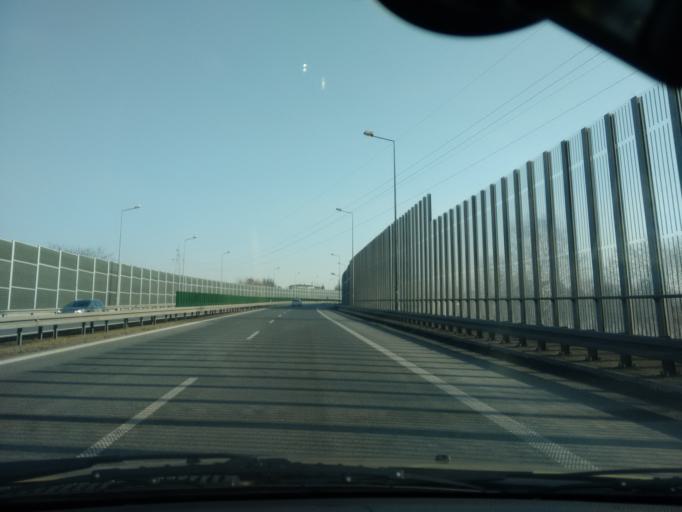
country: PL
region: Silesian Voivodeship
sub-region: Bielsko-Biala
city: Bielsko-Biala
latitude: 49.8493
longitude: 19.0528
